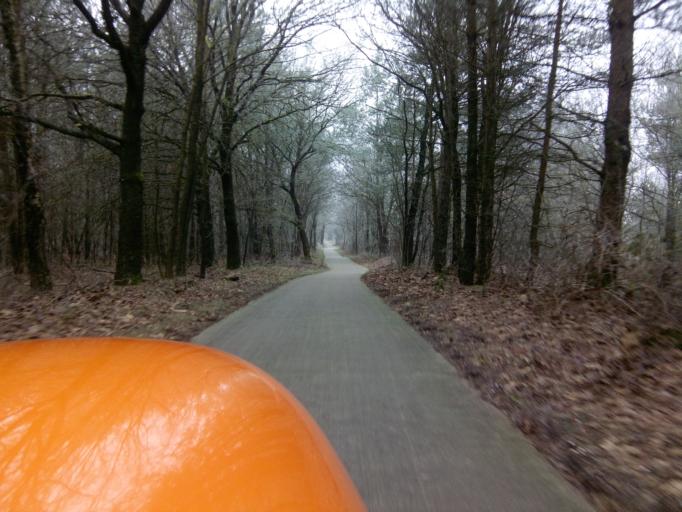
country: NL
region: Gelderland
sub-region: Gemeente Barneveld
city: Garderen
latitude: 52.2456
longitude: 5.7326
